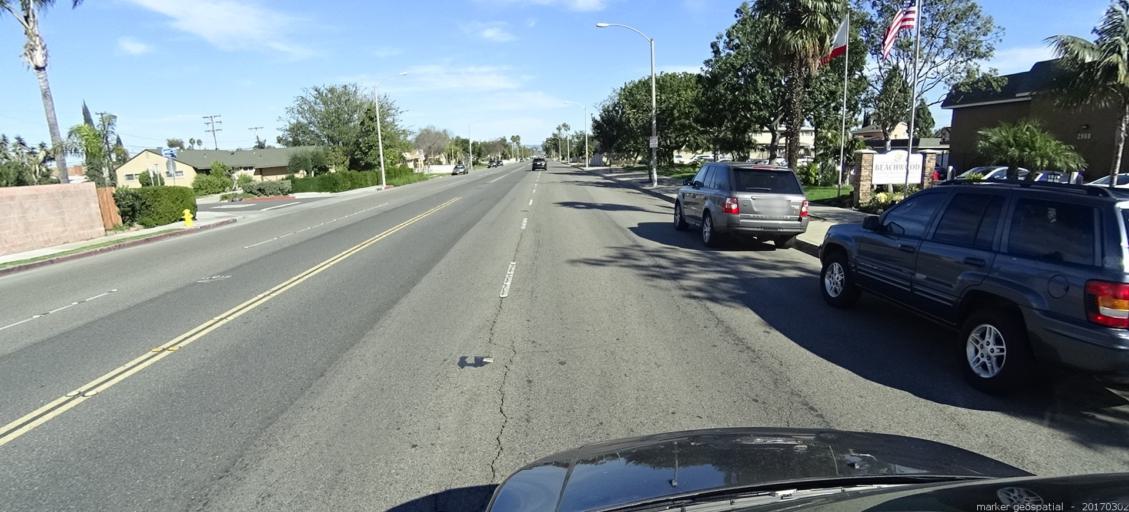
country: US
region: California
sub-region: Orange County
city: Stanton
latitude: 33.8247
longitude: -117.9923
